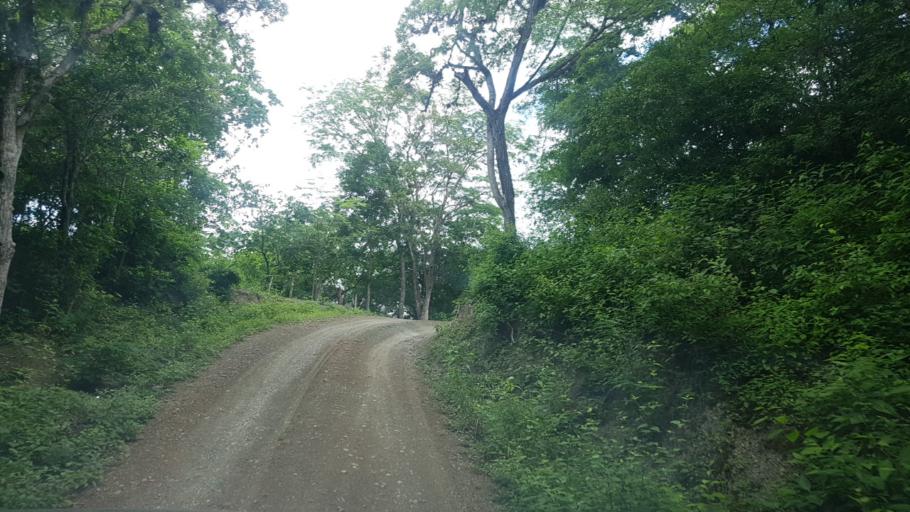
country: NI
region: Nueva Segovia
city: Mozonte
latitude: 13.5868
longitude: -86.3951
